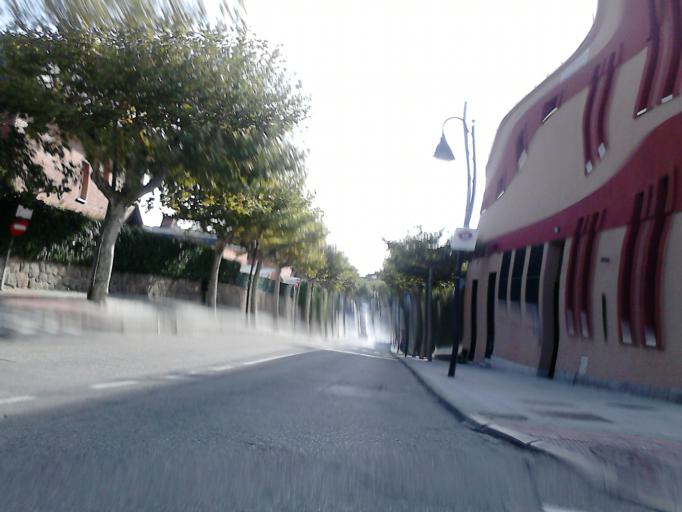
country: ES
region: Madrid
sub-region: Provincia de Madrid
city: Galapagar
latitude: 40.5810
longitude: -4.0079
